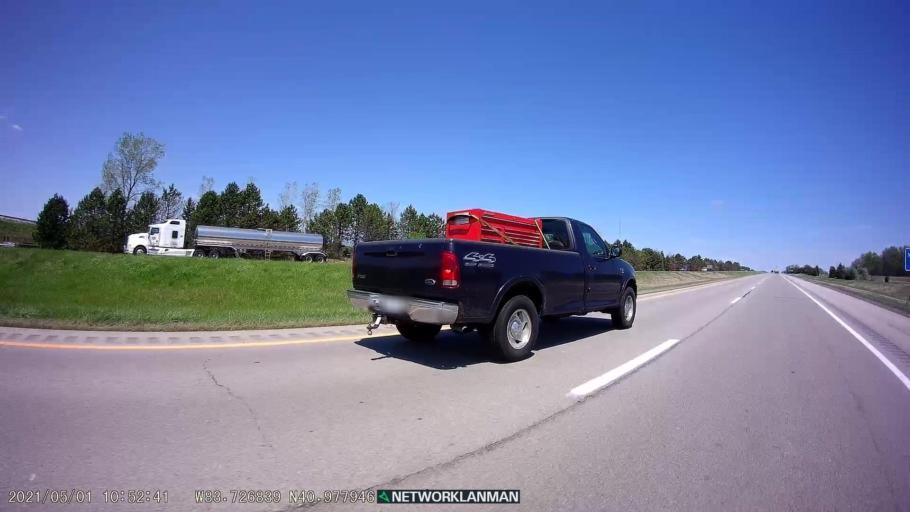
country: US
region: Ohio
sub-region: Hancock County
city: Findlay
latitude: 40.9781
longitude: -83.7258
